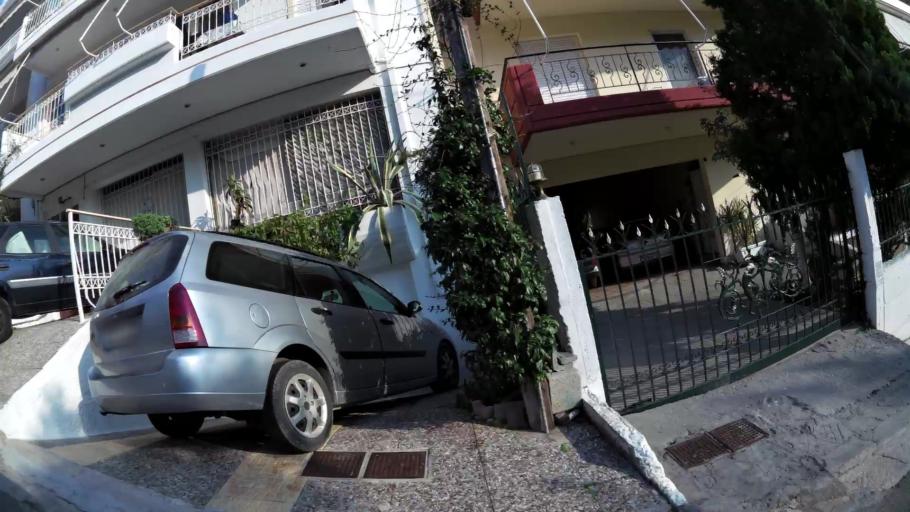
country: GR
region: Attica
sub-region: Nomarchia Athinas
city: Petroupolis
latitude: 38.0477
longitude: 23.6771
